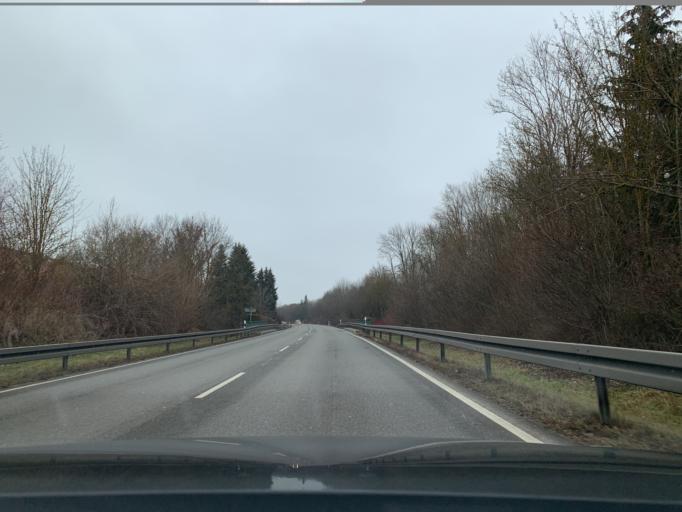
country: DE
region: Baden-Wuerttemberg
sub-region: Freiburg Region
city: Villingen-Schwenningen
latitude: 48.0617
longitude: 8.4702
